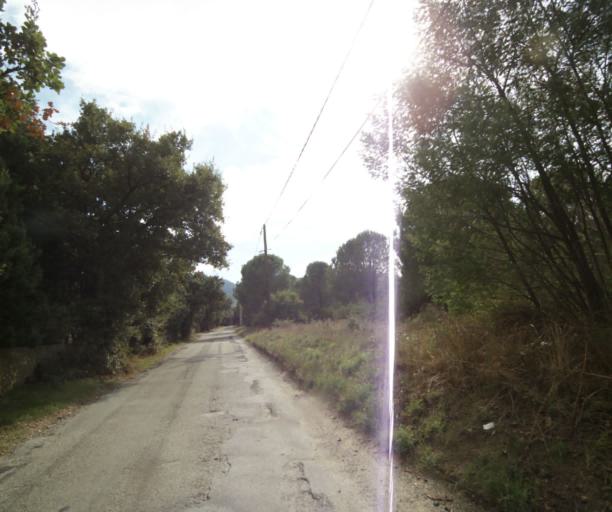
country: FR
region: Languedoc-Roussillon
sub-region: Departement des Pyrenees-Orientales
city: Sant Andreu de Sureda
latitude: 42.5463
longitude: 2.9906
